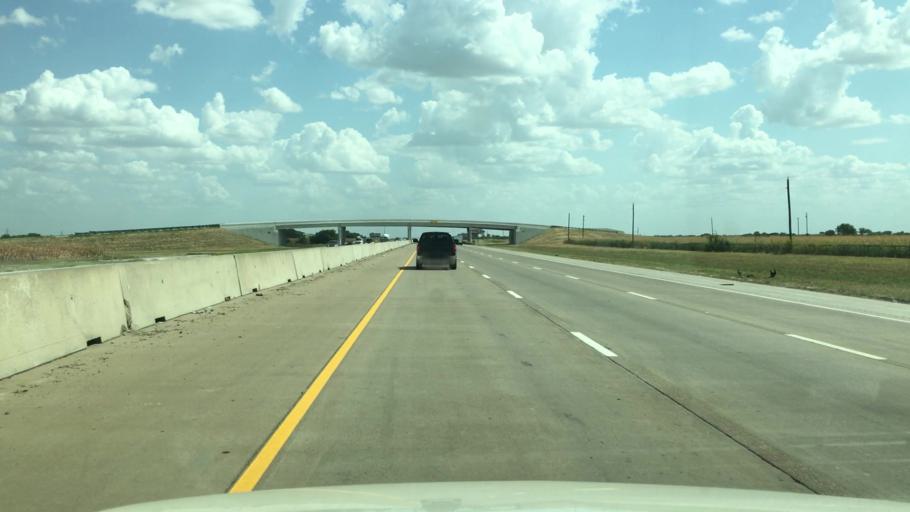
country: US
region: Texas
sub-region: Ellis County
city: Waxahachie
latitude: 32.3253
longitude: -96.8595
